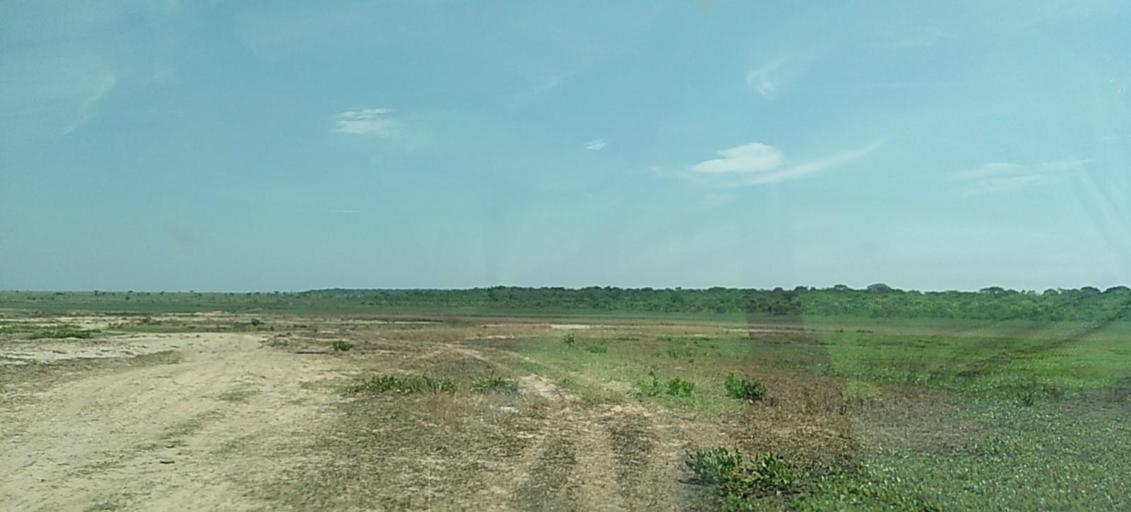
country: ZM
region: North-Western
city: Mwinilunga
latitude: -11.6705
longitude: 25.2064
